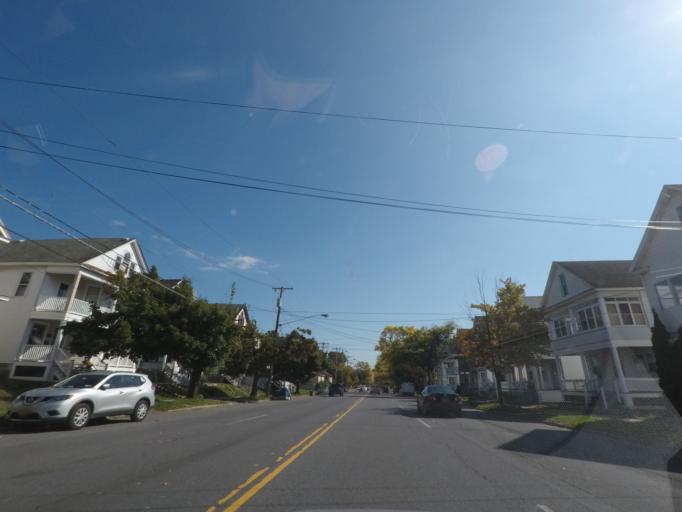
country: US
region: New York
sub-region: Albany County
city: West Albany
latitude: 42.6697
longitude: -73.7857
